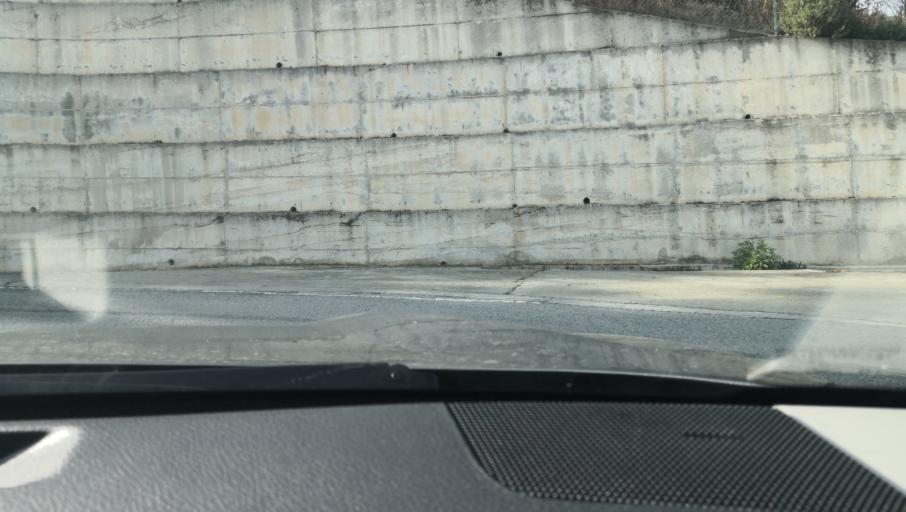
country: CY
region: Lefkosia
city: Lefka
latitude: 35.0231
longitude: 32.7225
